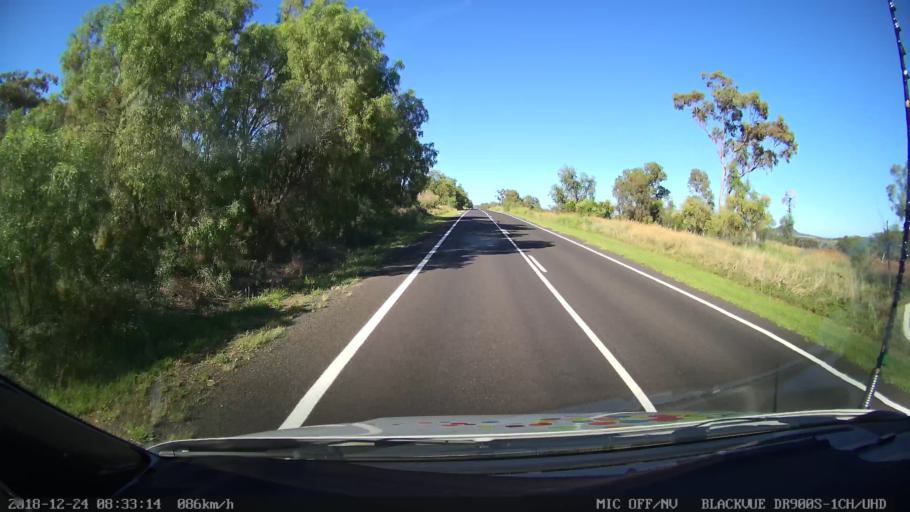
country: AU
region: New South Wales
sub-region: Tamworth Municipality
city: Phillip
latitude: -31.2850
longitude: 150.6872
